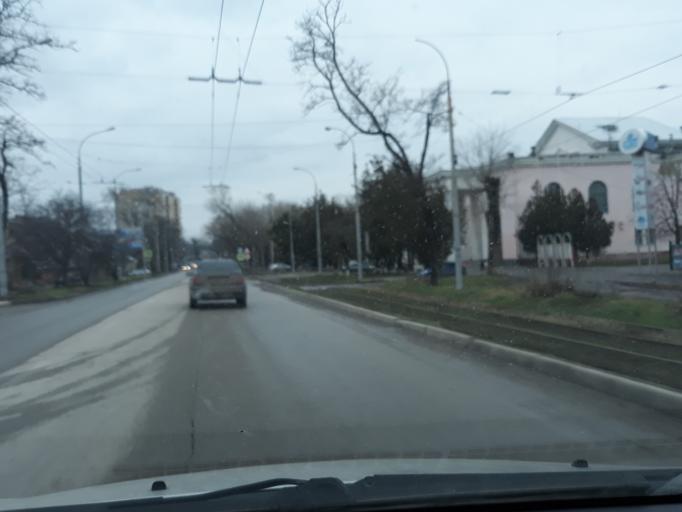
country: RU
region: Rostov
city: Taganrog
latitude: 47.2300
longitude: 38.9066
